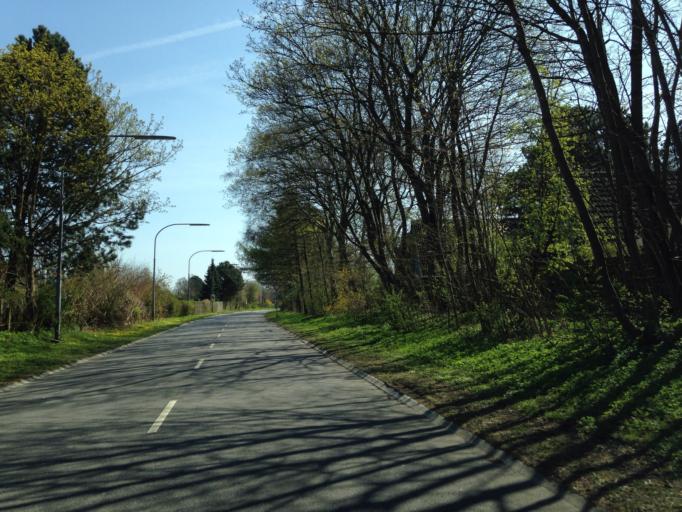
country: DK
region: Zealand
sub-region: Greve Kommune
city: Greve
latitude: 55.5736
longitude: 12.2846
